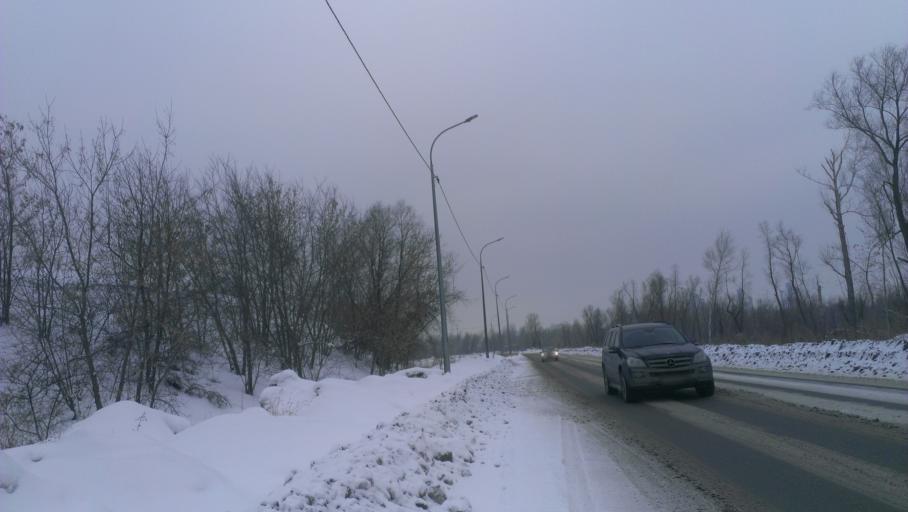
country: RU
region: Altai Krai
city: Zaton
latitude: 53.3197
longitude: 83.8167
